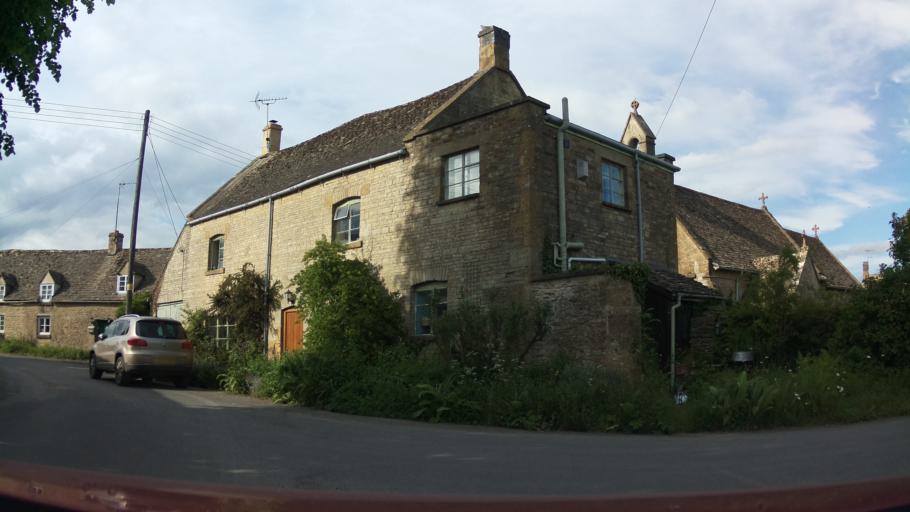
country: GB
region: England
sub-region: Gloucestershire
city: Donnington
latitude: 51.9531
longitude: -1.7813
